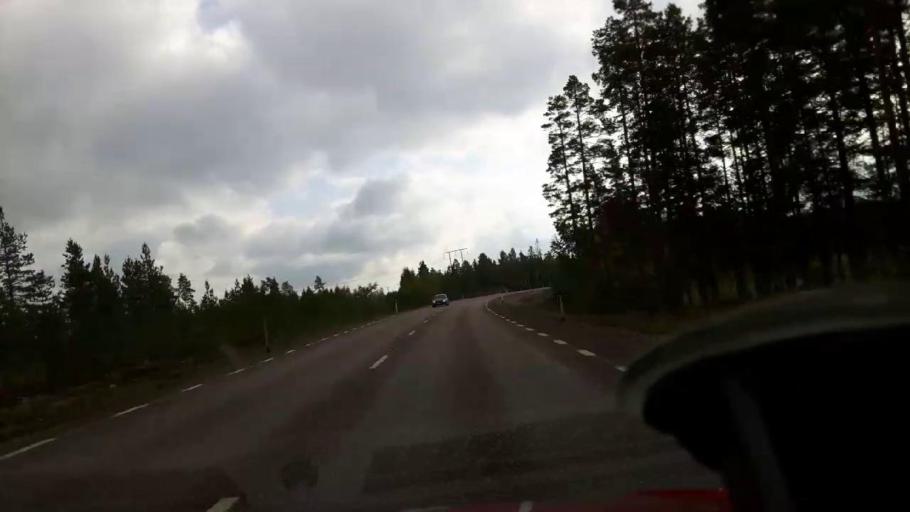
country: SE
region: Gaevleborg
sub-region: Soderhamns Kommun
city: Ljusne
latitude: 61.0986
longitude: 16.9514
